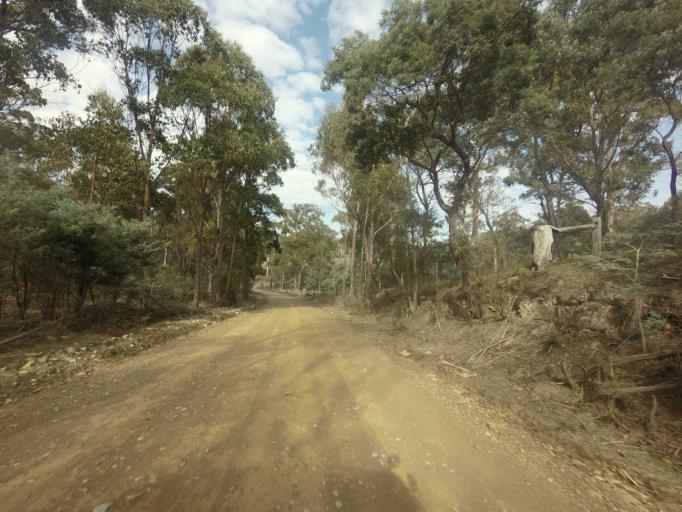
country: AU
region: Tasmania
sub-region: Sorell
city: Sorell
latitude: -42.5637
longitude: 147.4679
